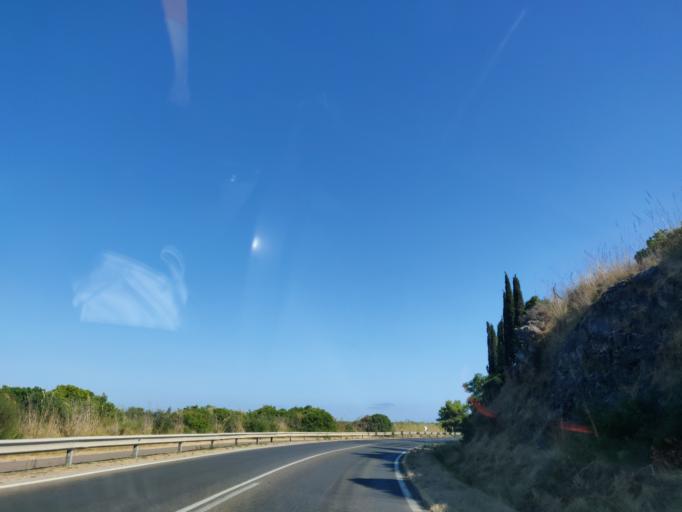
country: IT
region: Tuscany
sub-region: Provincia di Grosseto
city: Porto Ercole
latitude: 42.4240
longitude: 11.2012
